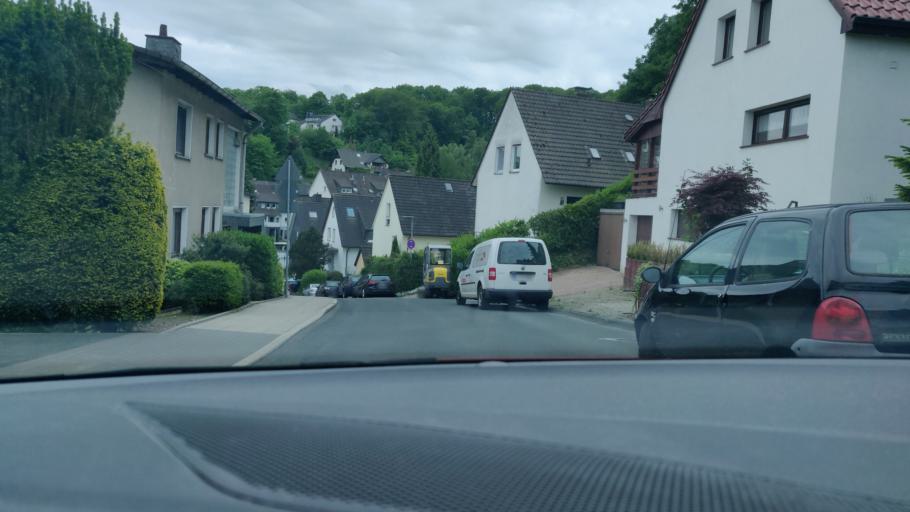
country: DE
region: North Rhine-Westphalia
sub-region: Regierungsbezirk Dusseldorf
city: Velbert
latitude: 51.3117
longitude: 7.0800
